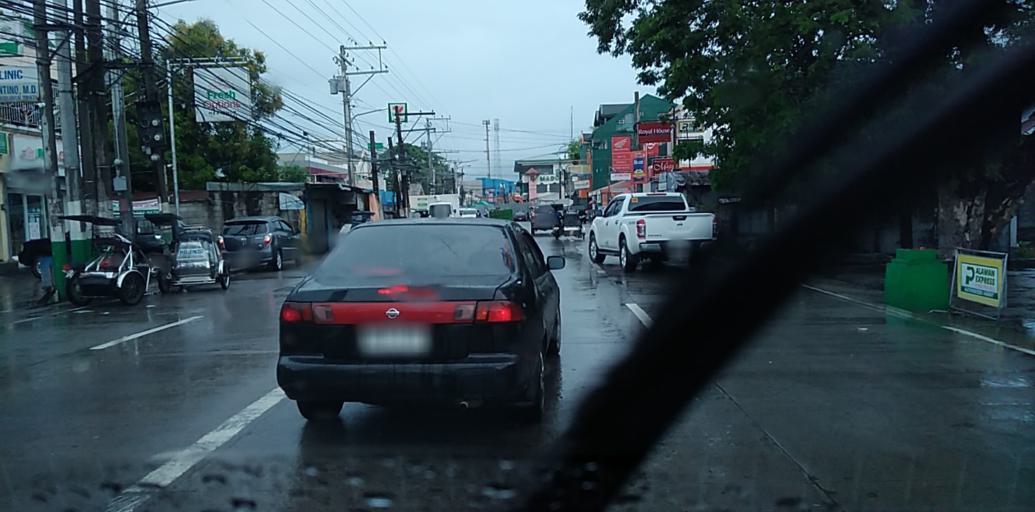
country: PH
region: Central Luzon
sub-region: Province of Pampanga
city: Mexico
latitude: 15.0633
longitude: 120.7202
